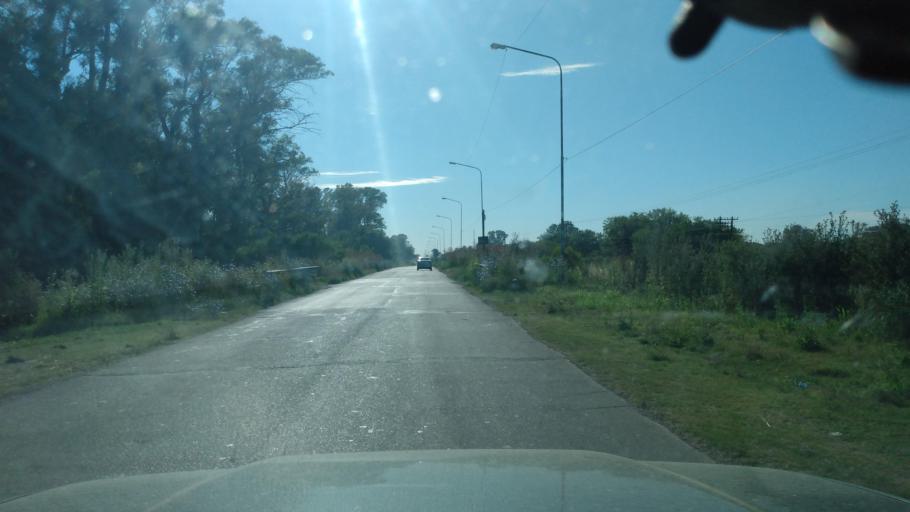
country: AR
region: Buenos Aires
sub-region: Partido de Lujan
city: Lujan
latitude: -34.5812
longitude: -59.0697
